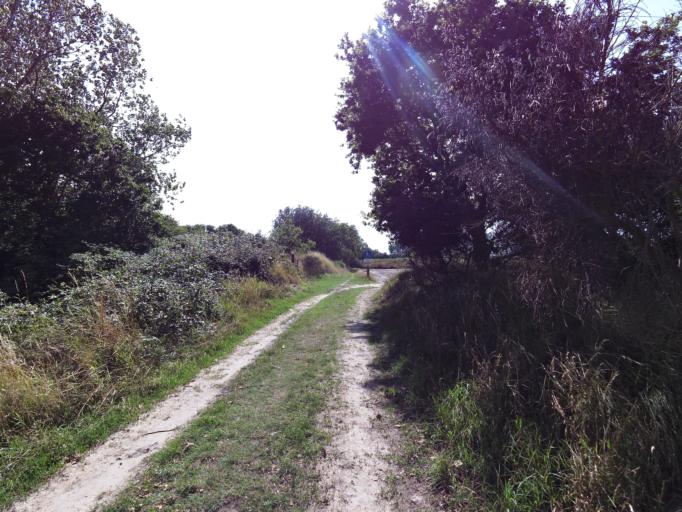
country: NL
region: South Holland
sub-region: Gemeente Goeree-Overflakkee
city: Ouddorp
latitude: 51.8048
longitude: 3.9262
